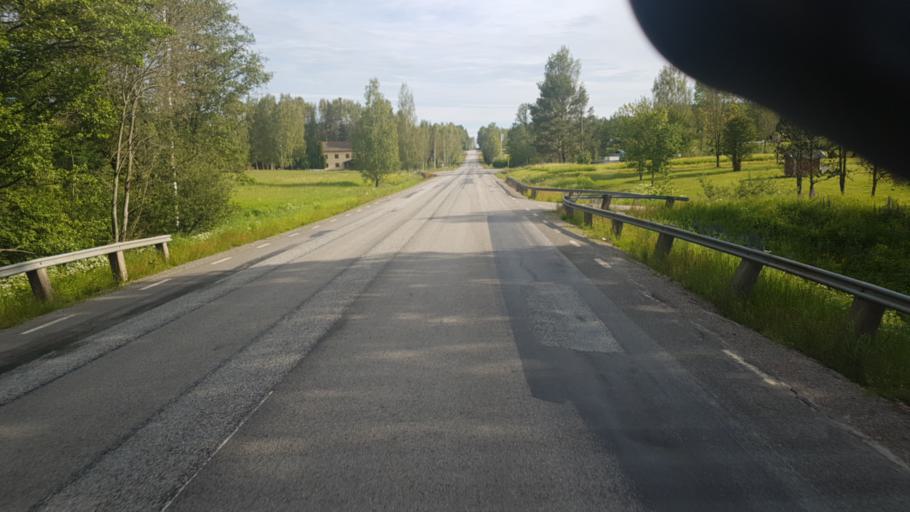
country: SE
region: Vaermland
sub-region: Arvika Kommun
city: Arvika
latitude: 59.6816
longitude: 12.6311
